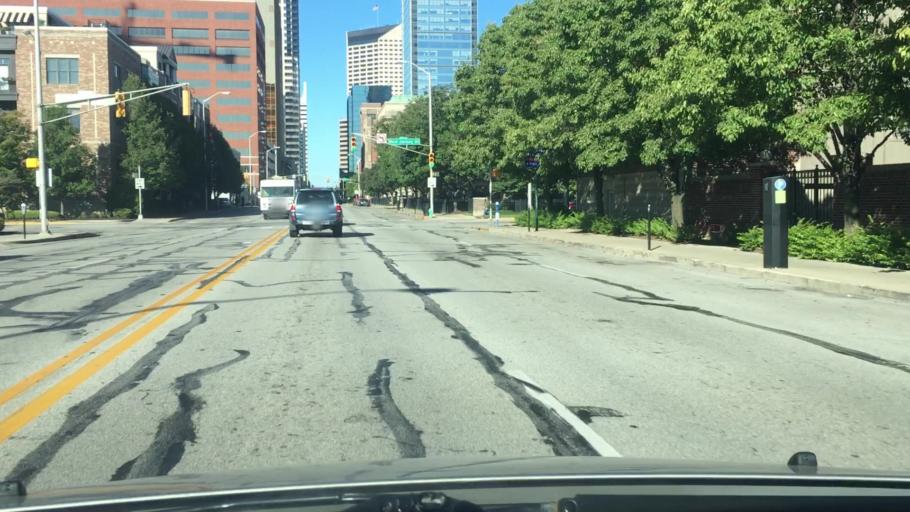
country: US
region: Indiana
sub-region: Marion County
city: Indianapolis
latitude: 39.7698
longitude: -86.1502
